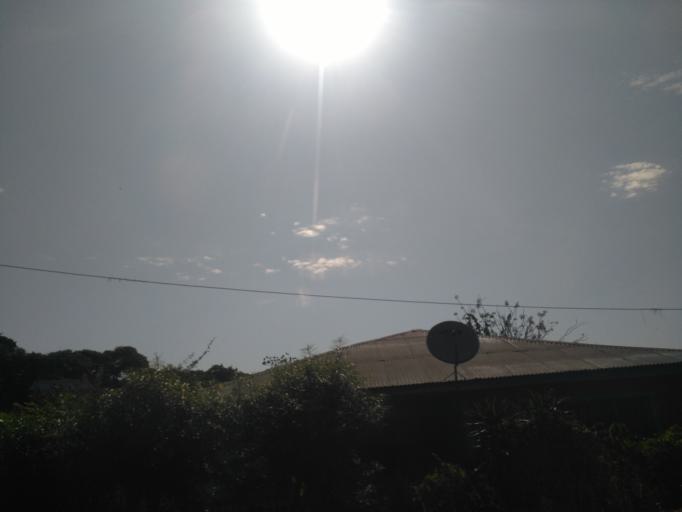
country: TZ
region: Mwanza
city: Mwanza
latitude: -2.4930
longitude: 32.8979
